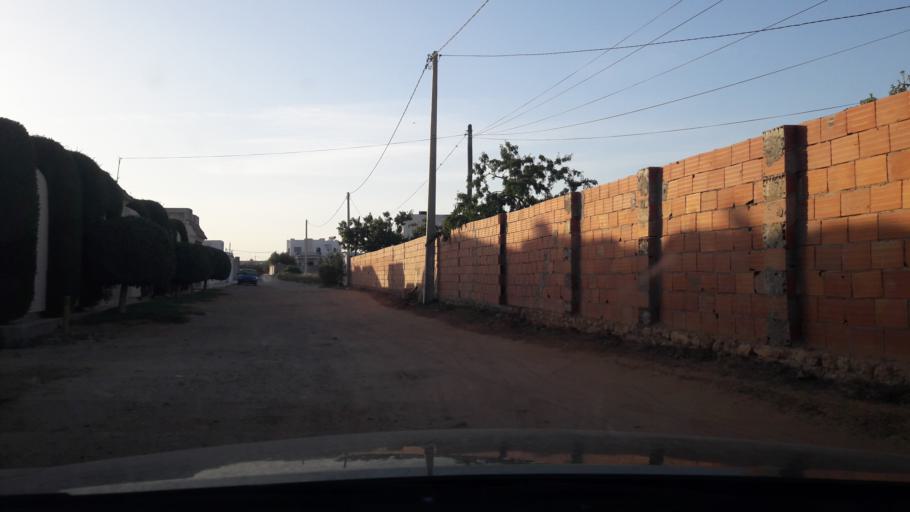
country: TN
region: Safaqis
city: Al Qarmadah
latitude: 34.7931
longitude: 10.7530
